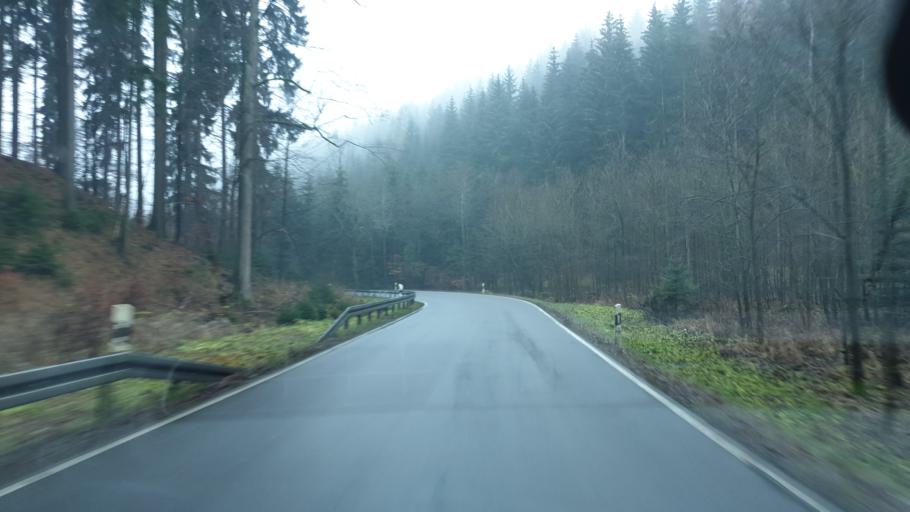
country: DE
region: Saxony
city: Seiffen
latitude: 50.6308
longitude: 13.4156
